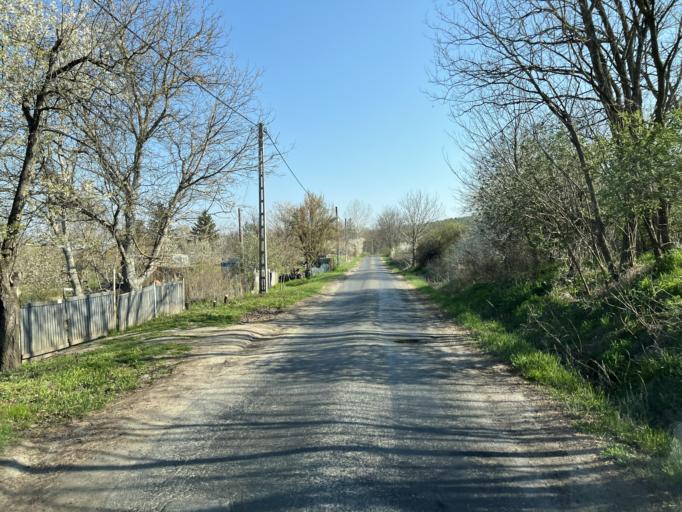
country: SK
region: Nitriansky
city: Sahy
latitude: 47.9914
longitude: 18.8159
